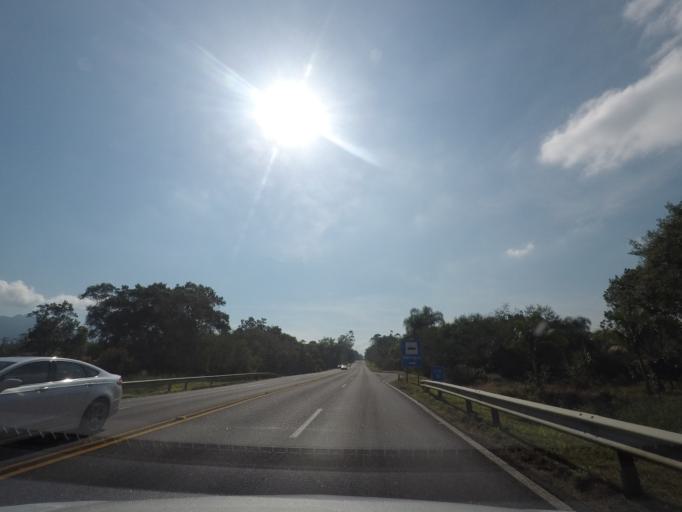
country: BR
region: Parana
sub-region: Pontal Do Parana
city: Pontal do Parana
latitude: -25.6123
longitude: -48.6041
